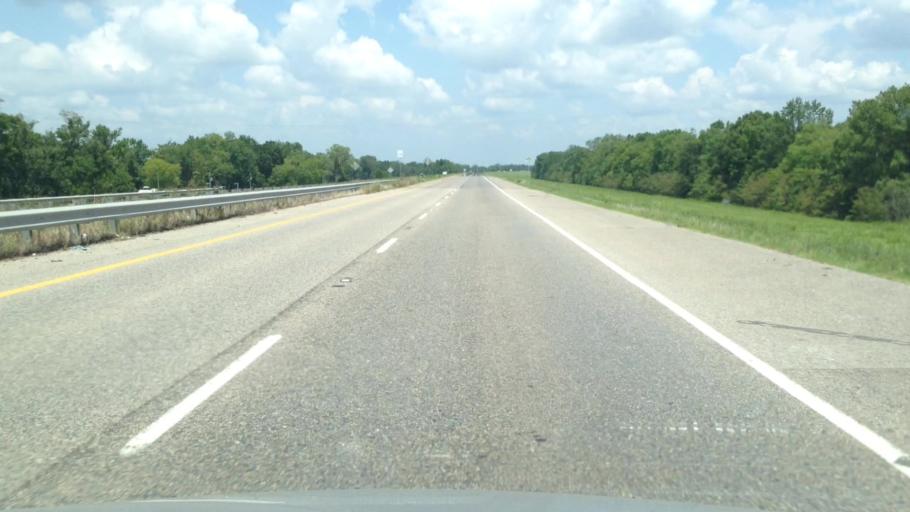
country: US
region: Louisiana
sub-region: Saint Landry Parish
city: Port Barre
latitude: 30.5479
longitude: -91.8599
